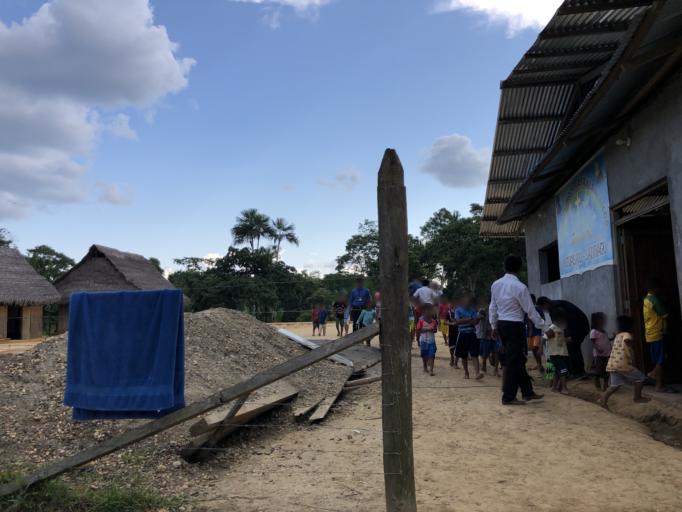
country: PE
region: Loreto
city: Puerto Galilea
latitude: -4.0592
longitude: -77.7600
